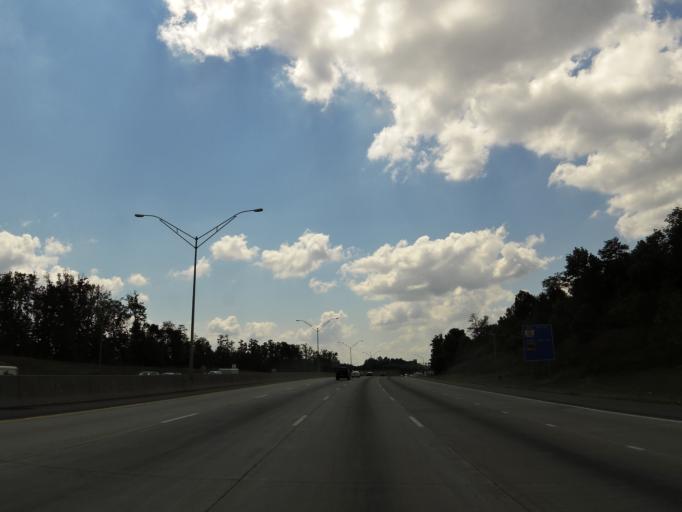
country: US
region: North Carolina
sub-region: Mecklenburg County
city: Charlotte
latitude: 35.2974
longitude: -80.7644
